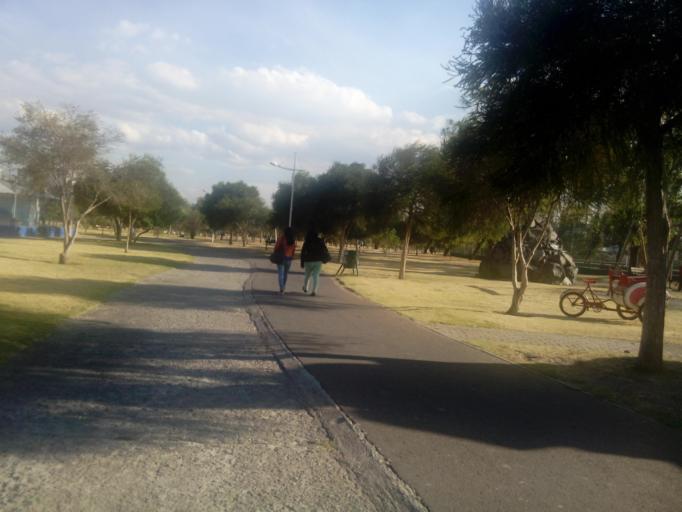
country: EC
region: Pichincha
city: Quito
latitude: -0.1796
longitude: -78.4842
